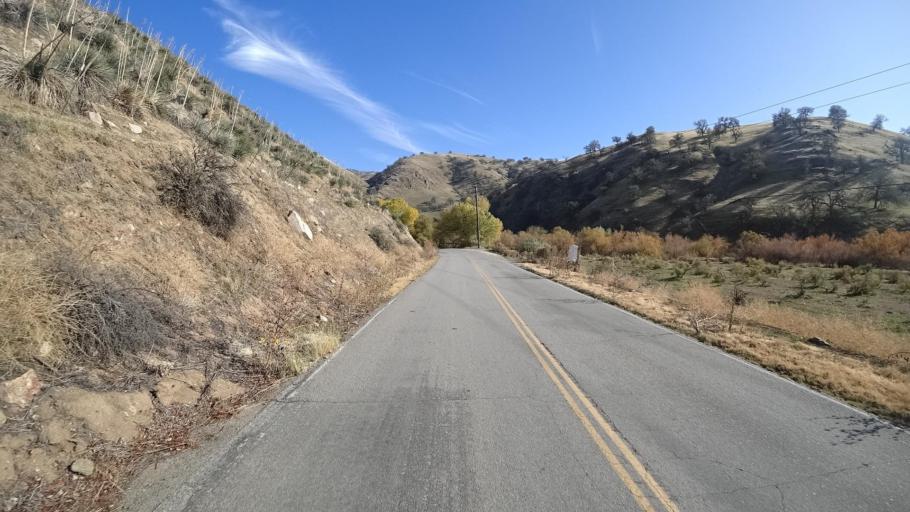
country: US
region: California
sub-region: Kern County
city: Bear Valley Springs
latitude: 35.2976
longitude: -118.6075
